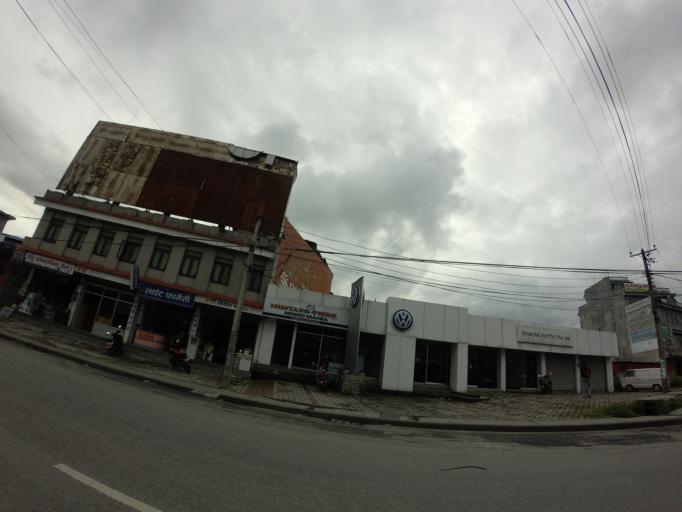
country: NP
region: Western Region
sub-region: Gandaki Zone
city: Pokhara
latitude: 28.2057
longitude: 83.9828
